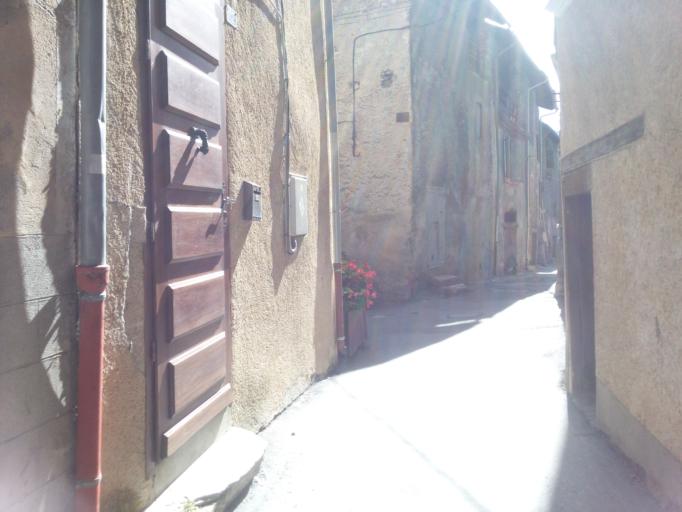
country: FR
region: Provence-Alpes-Cote d'Azur
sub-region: Departement des Hautes-Alpes
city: Guillestre
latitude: 44.6605
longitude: 6.6501
